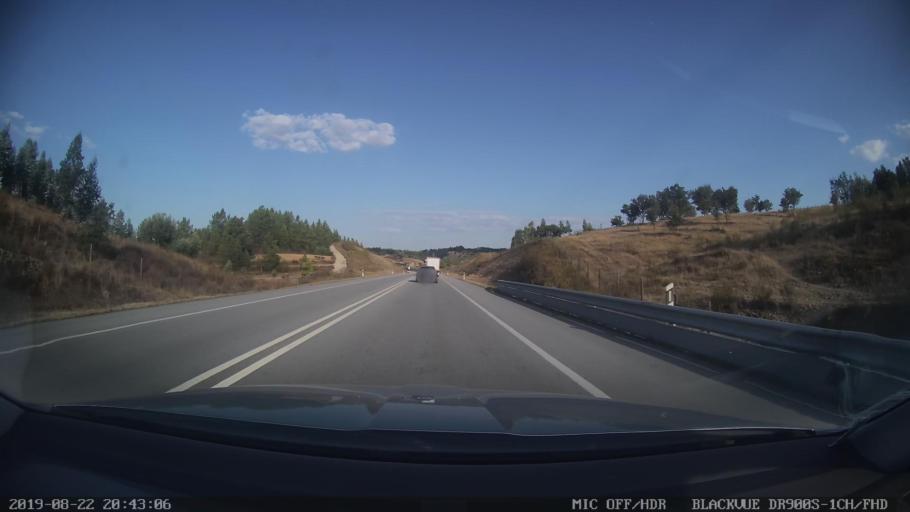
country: PT
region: Castelo Branco
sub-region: Proenca-A-Nova
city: Proenca-a-Nova
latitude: 39.6985
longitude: -7.8260
